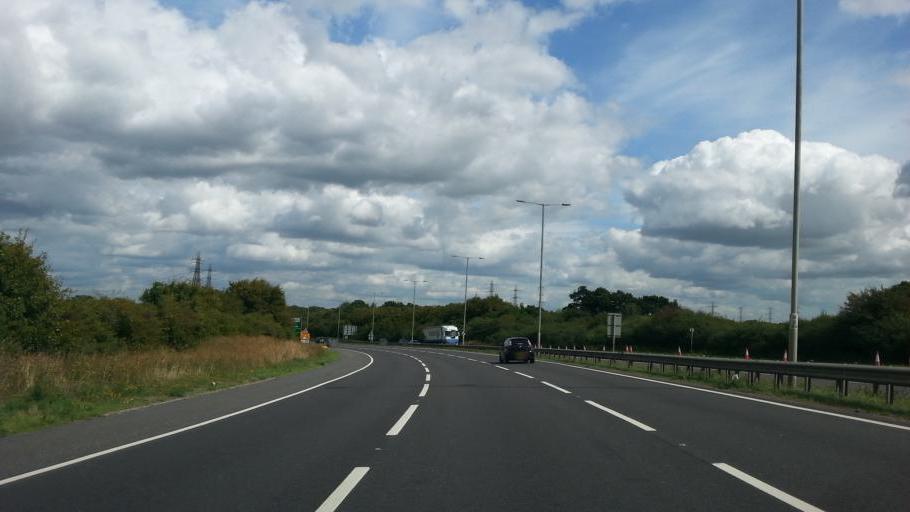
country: GB
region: England
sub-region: Essex
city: South Benfleet
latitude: 51.5844
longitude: 0.5648
